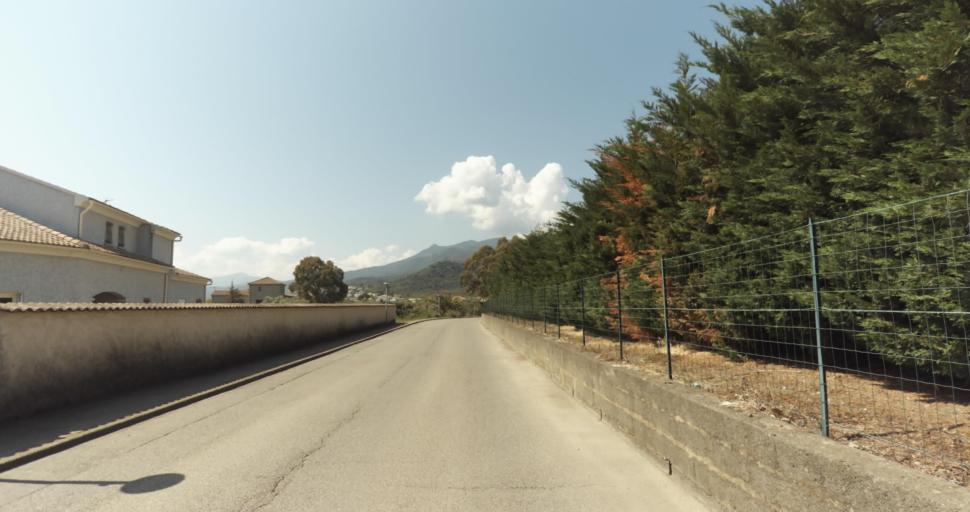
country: FR
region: Corsica
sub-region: Departement de la Haute-Corse
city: Biguglia
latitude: 42.6175
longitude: 9.4336
